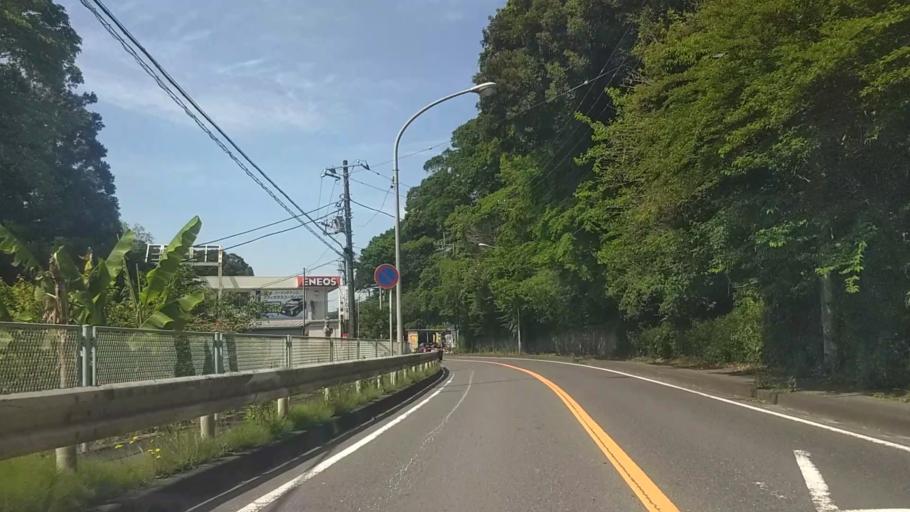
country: JP
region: Kanagawa
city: Kamakura
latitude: 35.3422
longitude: 139.5820
